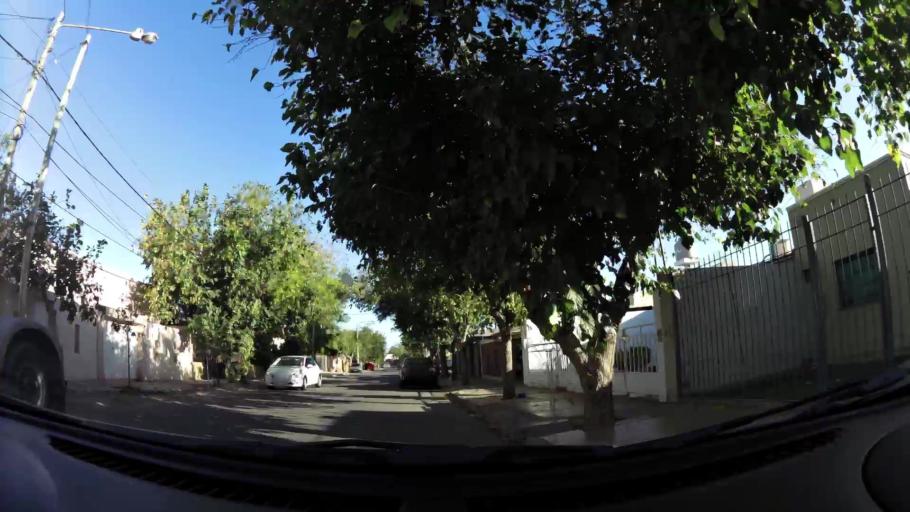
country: AR
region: San Juan
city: San Juan
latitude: -31.5502
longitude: -68.5178
